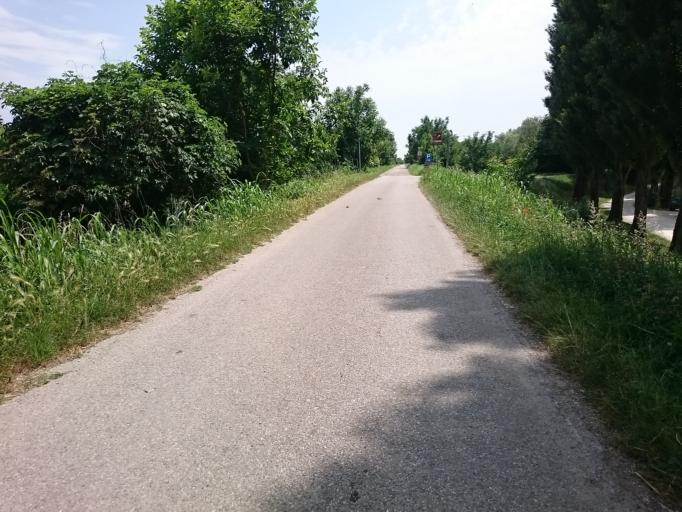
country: IT
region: Veneto
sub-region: Provincia di Venezia
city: Valli
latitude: 45.2292
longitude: 12.1416
